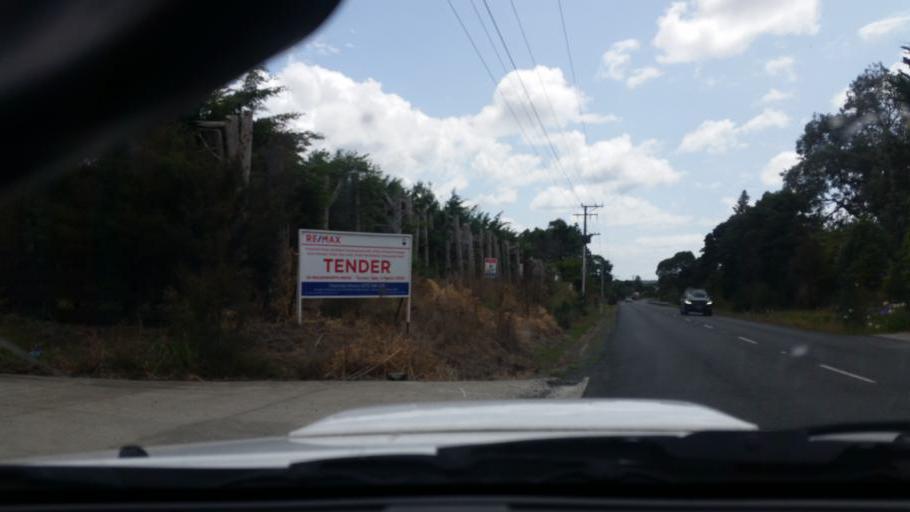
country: NZ
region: Auckland
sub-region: Auckland
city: Wellsford
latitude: -36.1203
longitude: 174.5725
